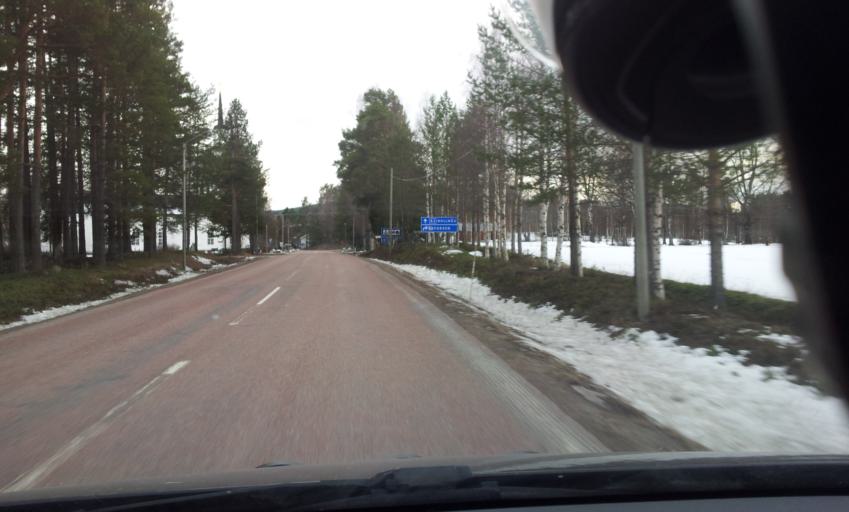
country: SE
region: Vaesternorrland
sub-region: Ange Kommun
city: Ange
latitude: 62.1866
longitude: 15.6557
